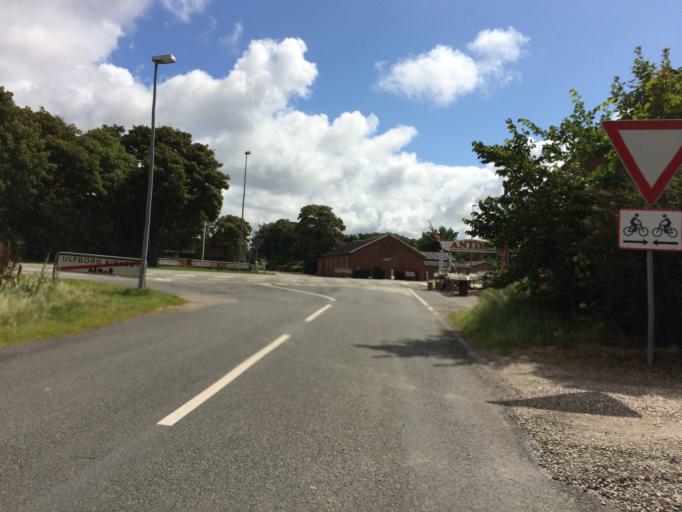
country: DK
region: Central Jutland
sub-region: Holstebro Kommune
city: Ulfborg
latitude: 56.3014
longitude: 8.3383
